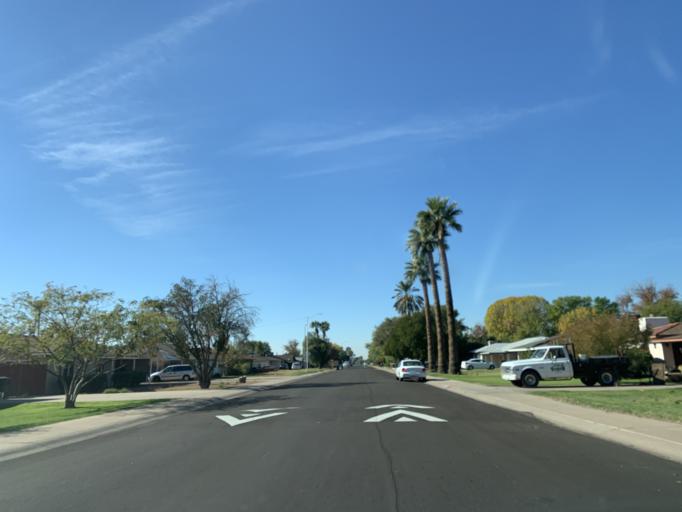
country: US
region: Arizona
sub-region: Maricopa County
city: Mesa
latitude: 33.4162
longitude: -111.8586
